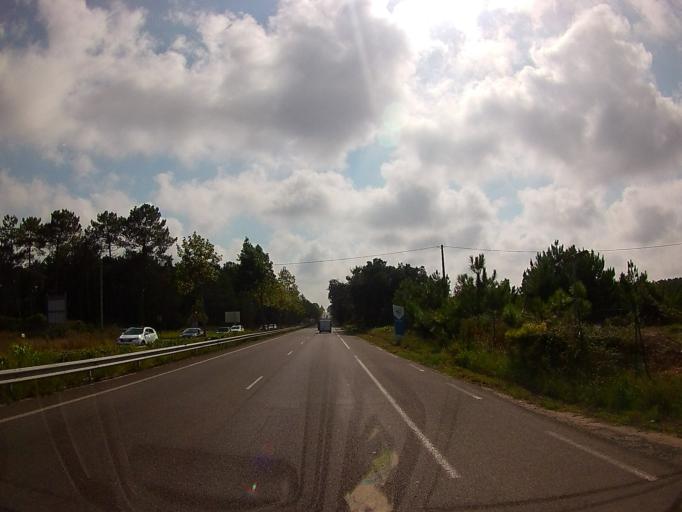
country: FR
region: Aquitaine
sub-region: Departement des Landes
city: Ondres
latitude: 43.5773
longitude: -1.4361
